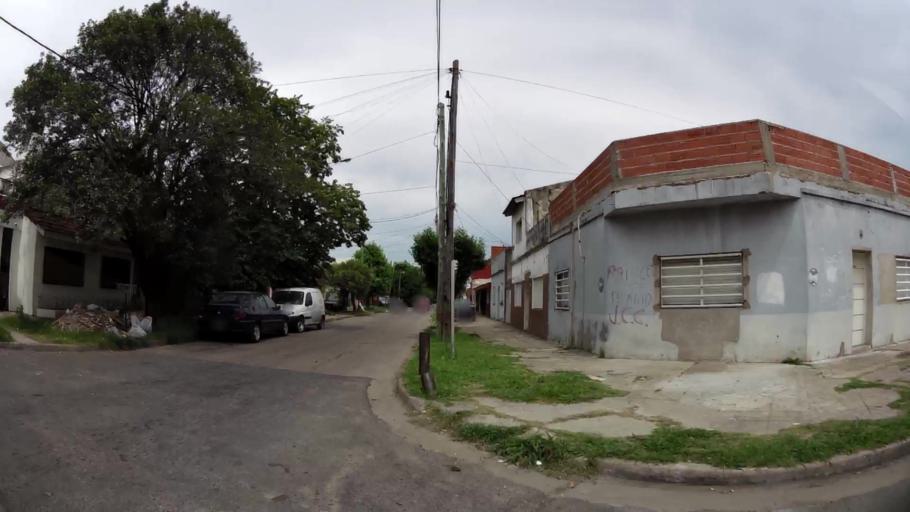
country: AR
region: Buenos Aires
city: San Justo
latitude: -34.6701
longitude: -58.5209
